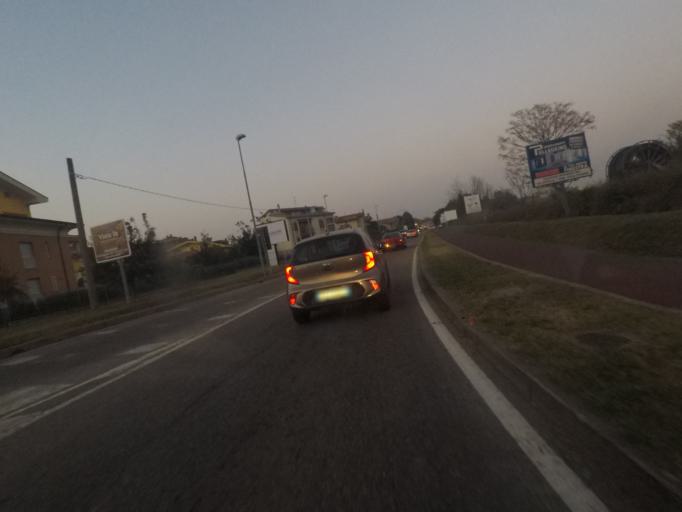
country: IT
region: Lombardy
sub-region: Provincia di Monza e Brianza
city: Brugherio
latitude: 45.5639
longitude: 9.3056
